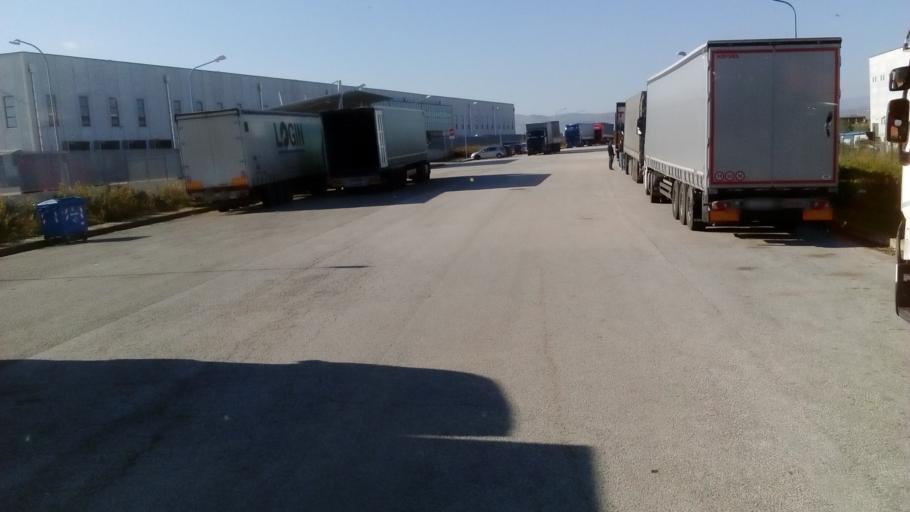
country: IT
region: Basilicate
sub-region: Provincia di Potenza
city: Melfi
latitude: 41.0782
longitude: 15.6544
